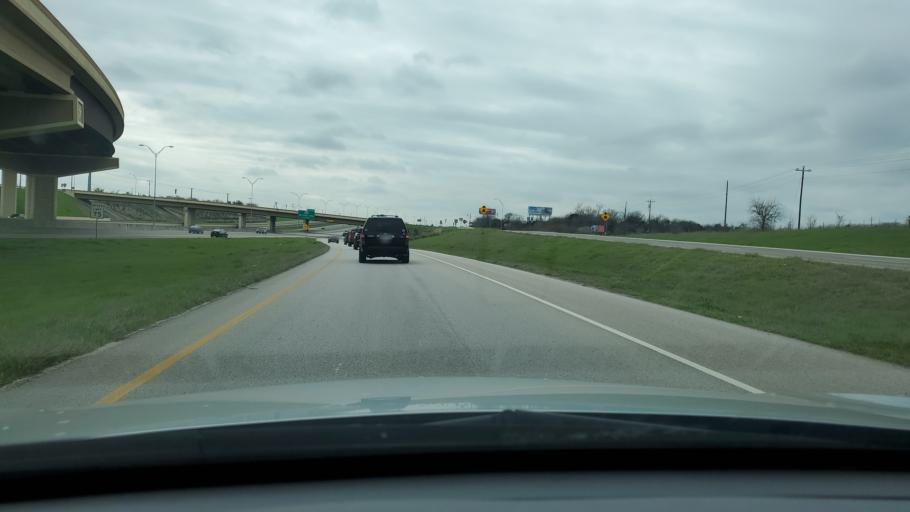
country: US
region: Texas
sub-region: Williamson County
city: Serenada
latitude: 30.6881
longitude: -97.6578
